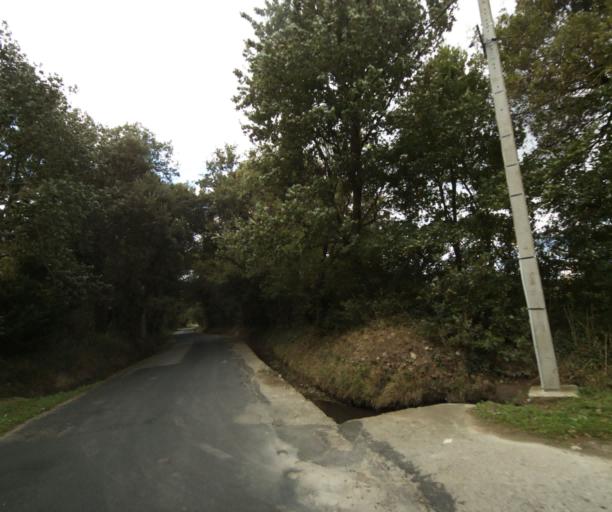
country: FR
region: Languedoc-Roussillon
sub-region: Departement des Pyrenees-Orientales
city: Argelers
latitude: 42.5601
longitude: 3.0273
